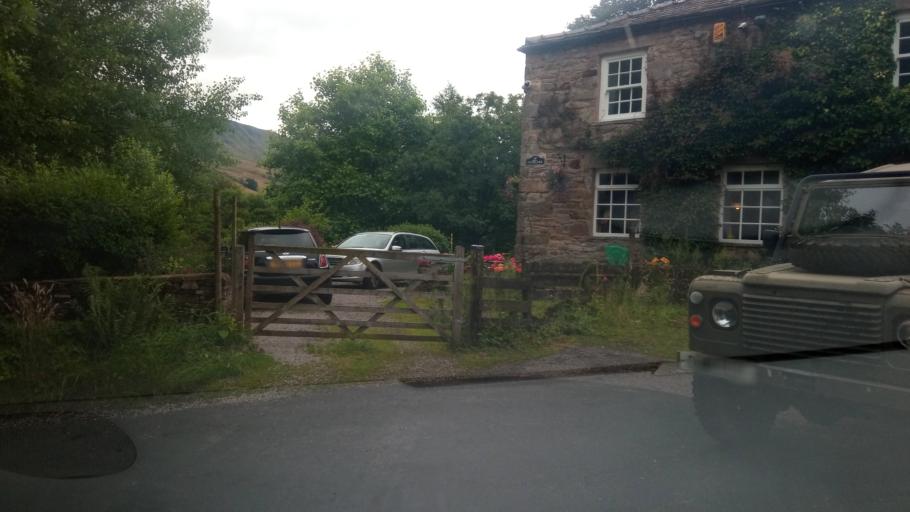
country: GB
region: England
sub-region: Cumbria
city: Kirkby Stephen
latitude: 54.4199
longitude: -2.3400
